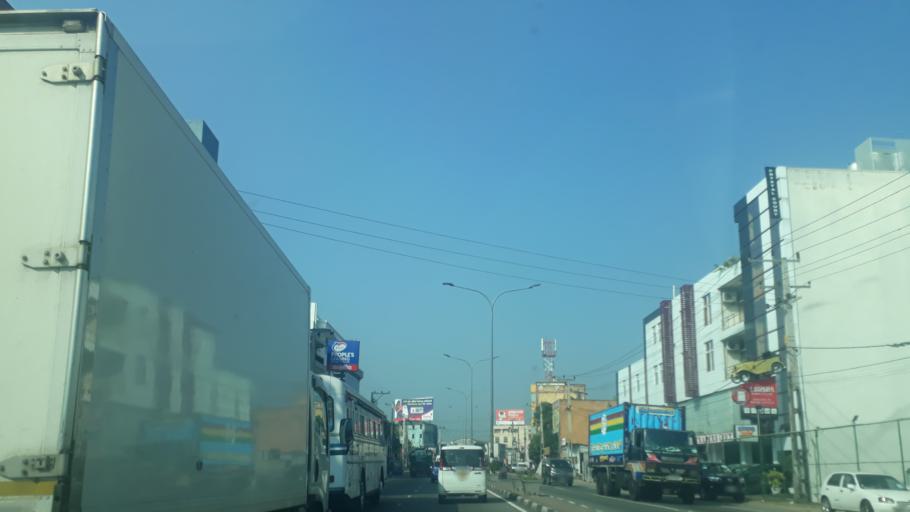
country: LK
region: Western
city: Kelaniya
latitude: 6.9679
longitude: 79.9096
